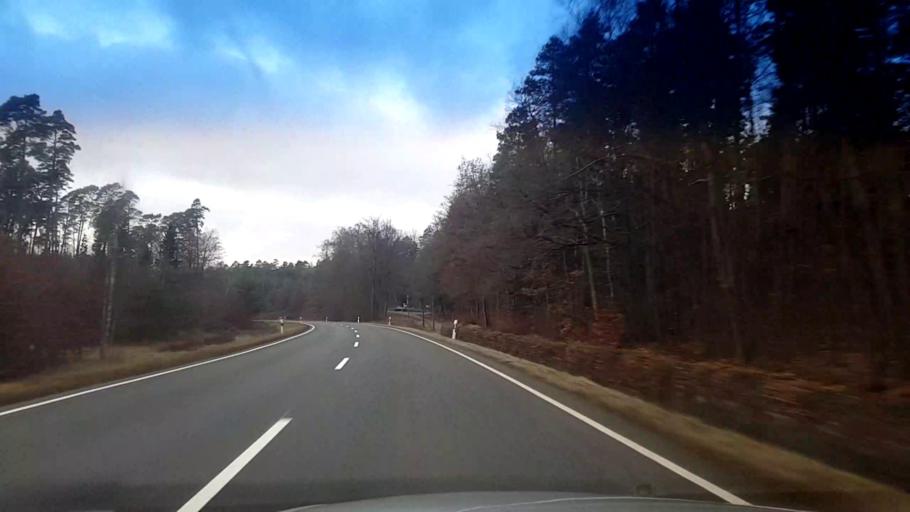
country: DE
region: Bavaria
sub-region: Upper Franconia
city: Memmelsdorf
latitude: 49.8896
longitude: 10.9680
